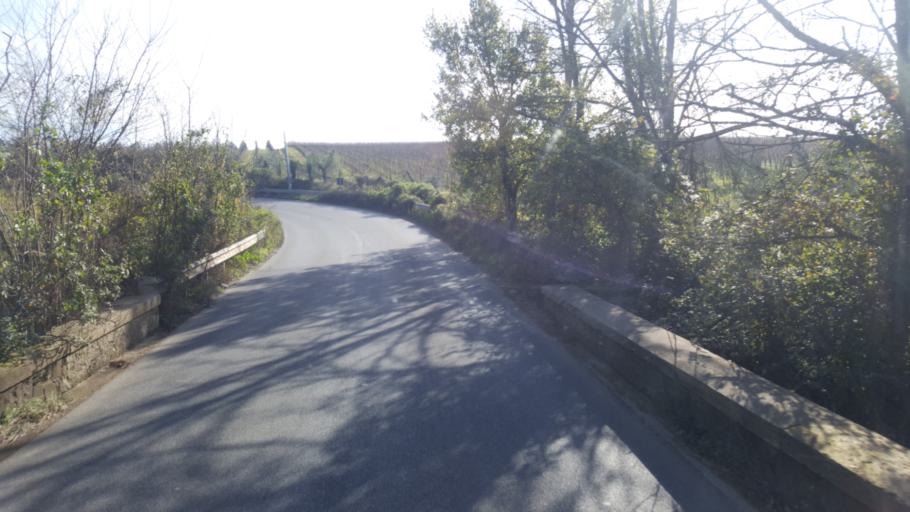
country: IT
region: Latium
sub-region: Citta metropolitana di Roma Capitale
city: Mantiglia di Ardea
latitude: 41.6886
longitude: 12.6036
